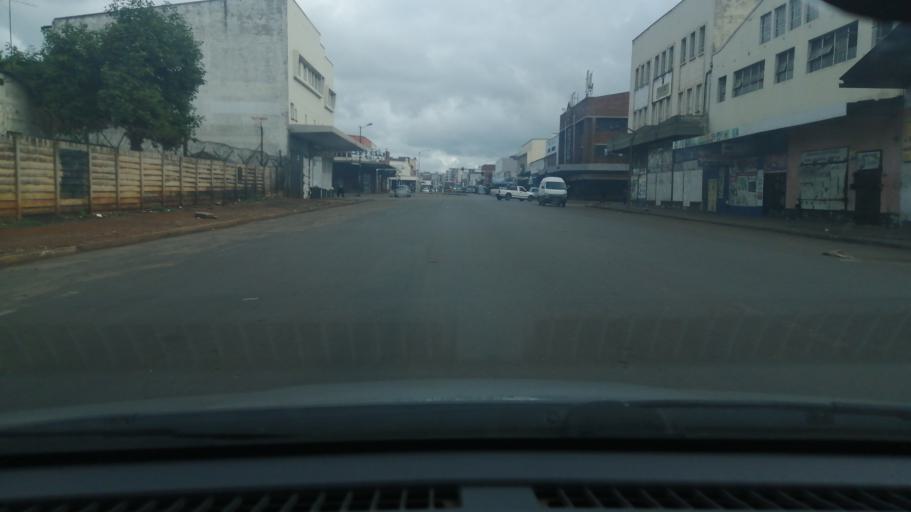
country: ZW
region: Harare
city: Harare
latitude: -17.8402
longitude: 31.0431
